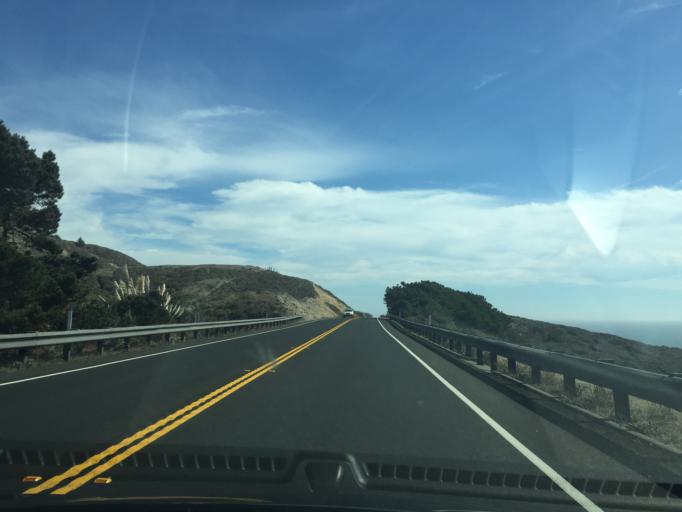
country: US
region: California
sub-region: Santa Cruz County
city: Bonny Doon
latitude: 37.0710
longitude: -122.2583
